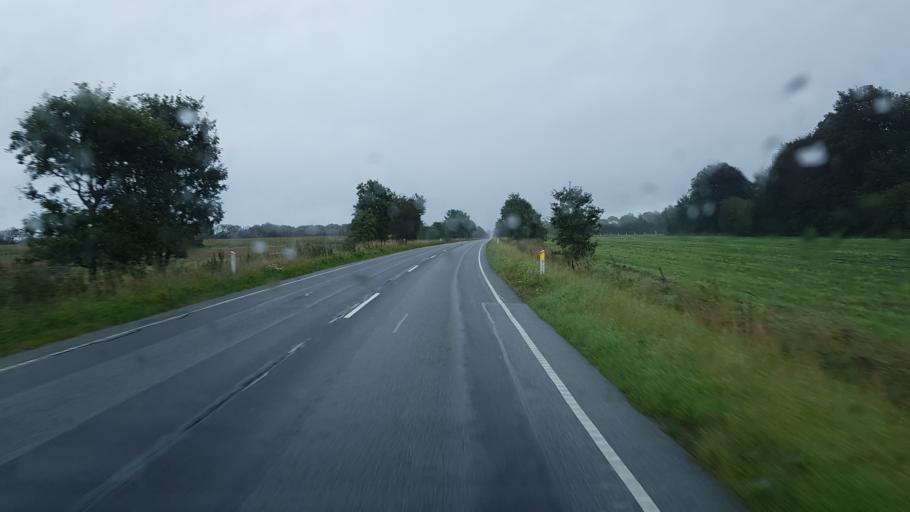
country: DK
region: South Denmark
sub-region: Kolding Kommune
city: Vamdrup
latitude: 55.3494
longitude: 9.2419
